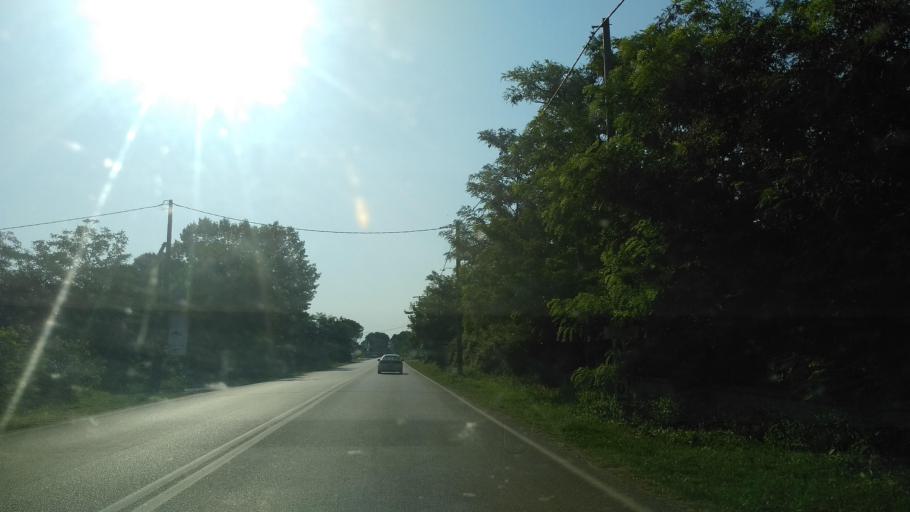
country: GR
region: Central Macedonia
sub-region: Nomos Thessalonikis
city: Stavros
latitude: 40.6692
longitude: 23.6719
